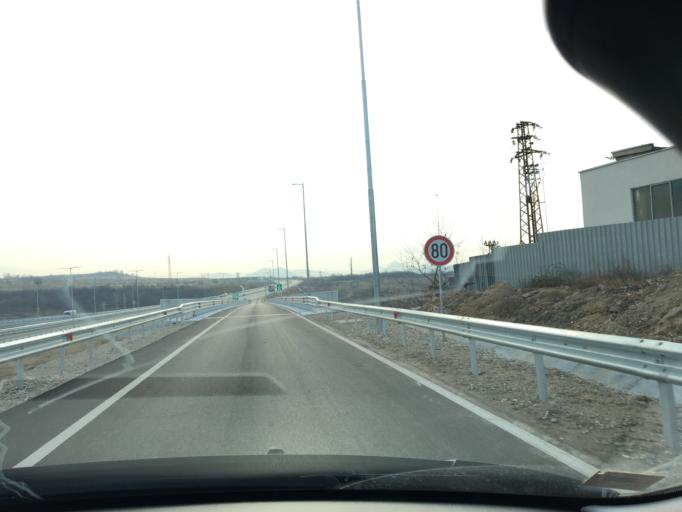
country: BG
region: Blagoevgrad
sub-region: Obshtina Sandanski
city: Sandanski
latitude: 41.5408
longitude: 23.2566
